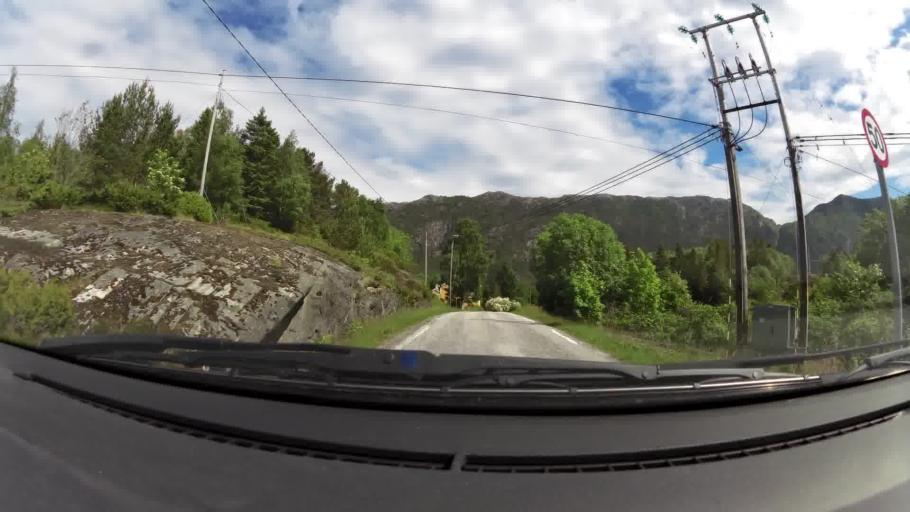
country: NO
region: More og Romsdal
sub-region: Kristiansund
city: Kristiansund
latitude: 63.0599
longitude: 7.7048
